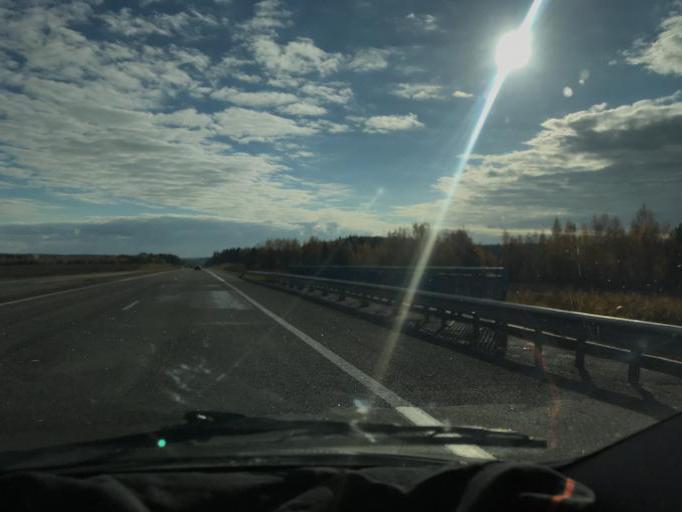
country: BY
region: Minsk
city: Lahoysk
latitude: 54.1482
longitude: 27.8098
